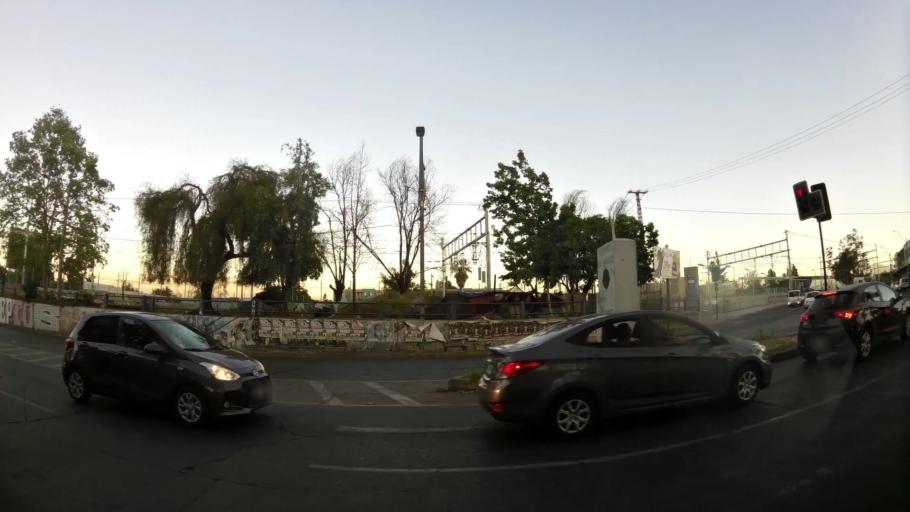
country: CL
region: Santiago Metropolitan
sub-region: Provincia de Maipo
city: San Bernardo
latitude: -33.5857
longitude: -70.6992
